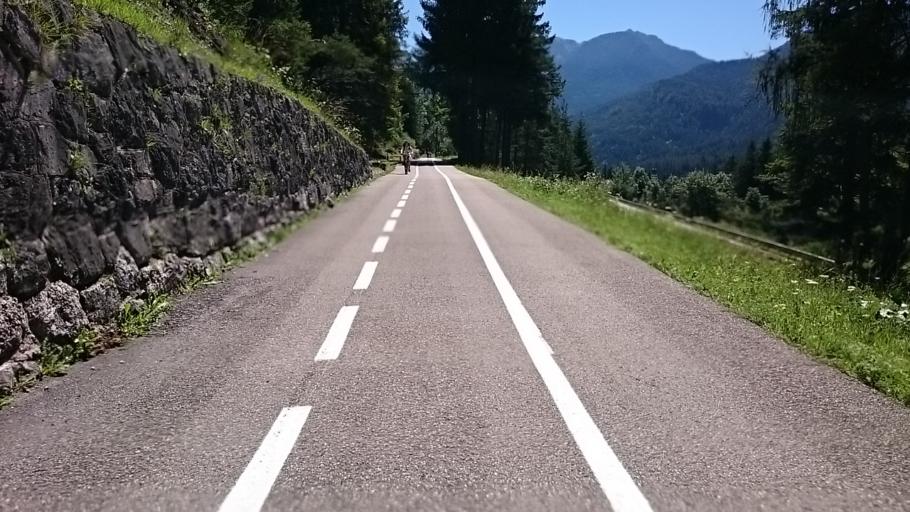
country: IT
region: Veneto
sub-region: Provincia di Belluno
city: Borca
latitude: 46.4416
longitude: 12.2155
